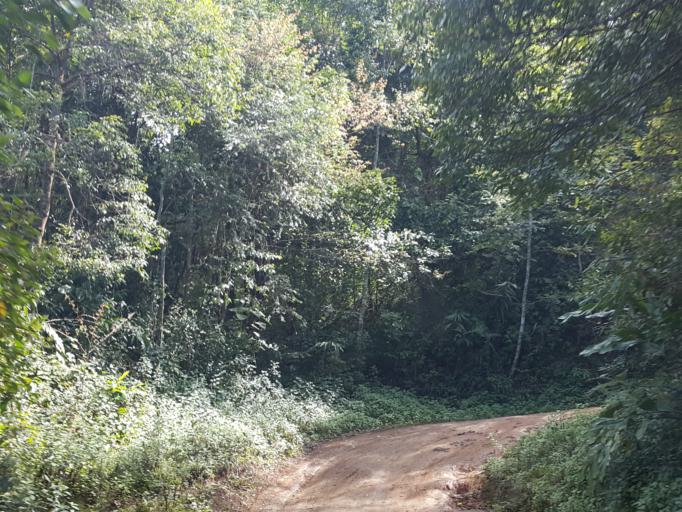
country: TH
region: Chiang Mai
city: Wiang Haeng
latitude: 19.5543
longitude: 98.8095
